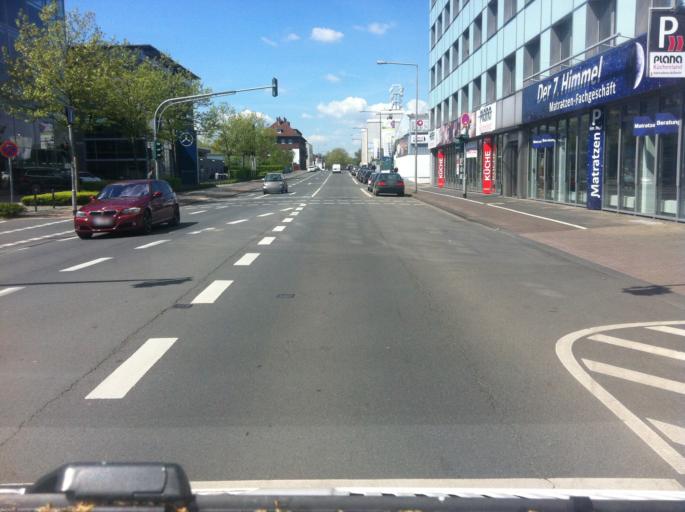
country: DE
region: North Rhine-Westphalia
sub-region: Regierungsbezirk Koln
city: Bilderstoeckchen
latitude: 50.9463
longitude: 6.8954
